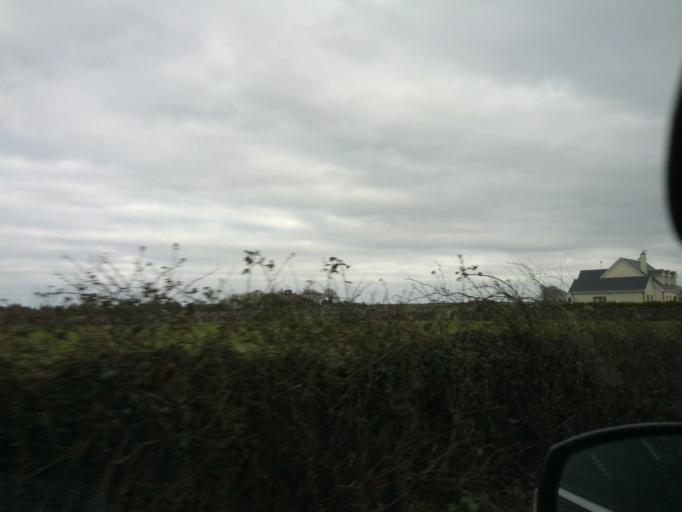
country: IE
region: Connaught
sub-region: County Galway
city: Oranmore
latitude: 53.1667
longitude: -8.8814
